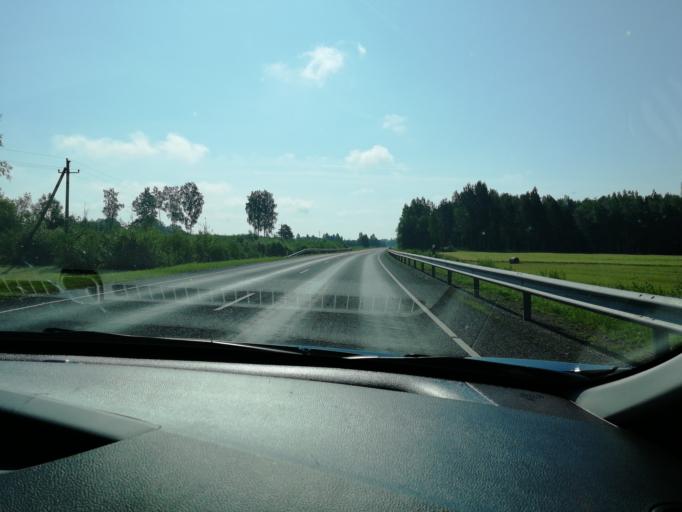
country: EE
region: Paernumaa
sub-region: Paikuse vald
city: Paikuse
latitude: 58.1998
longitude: 24.7372
